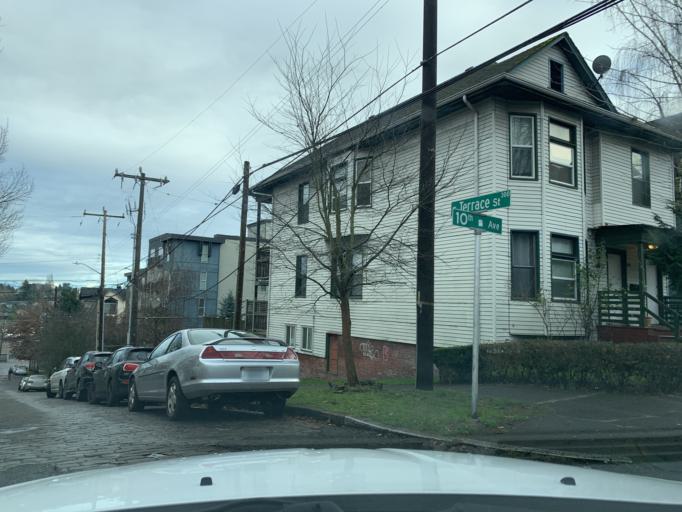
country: US
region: Washington
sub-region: King County
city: Seattle
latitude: 47.6053
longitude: -122.3194
